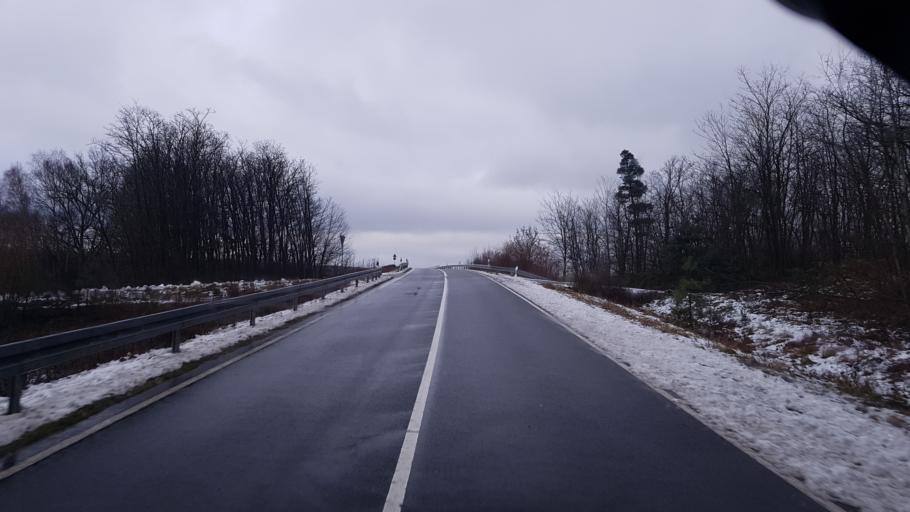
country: DE
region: Brandenburg
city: Schenkendobern
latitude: 51.8953
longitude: 14.6371
